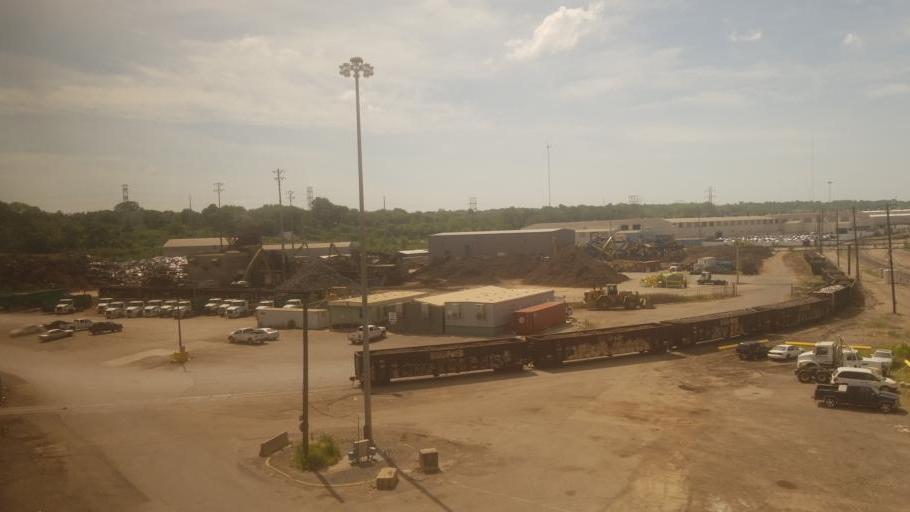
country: US
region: Missouri
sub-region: Jackson County
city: Sugar Creek
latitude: 39.1111
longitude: -94.4958
